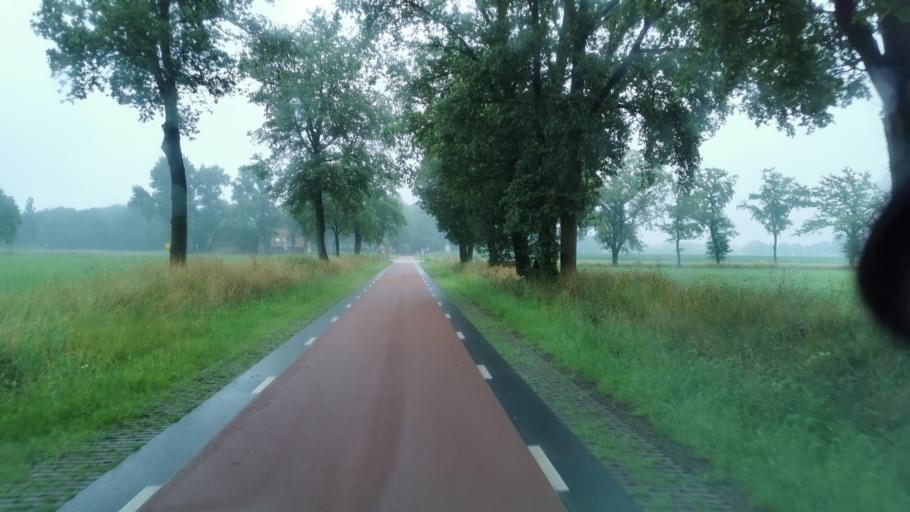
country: NL
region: Overijssel
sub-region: Gemeente Losser
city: Losser
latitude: 52.2494
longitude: 6.9808
